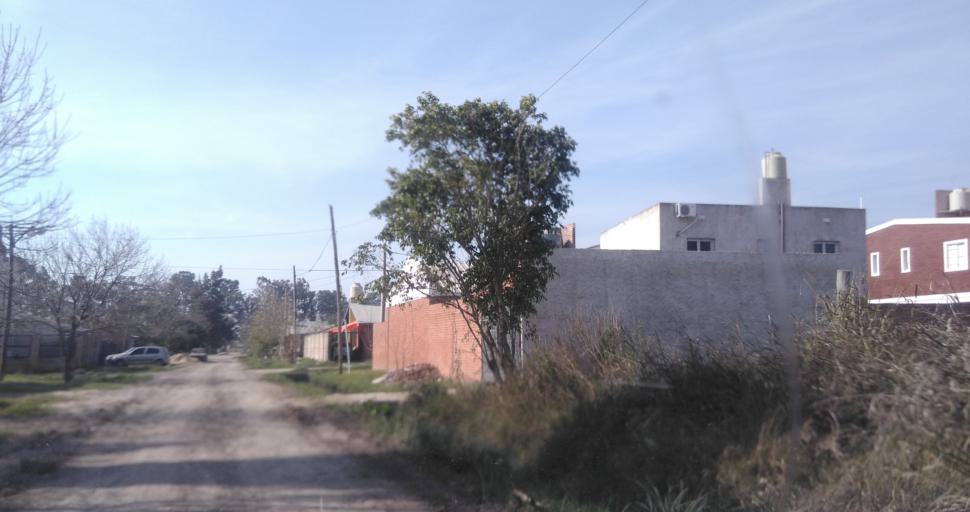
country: AR
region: Chaco
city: Fontana
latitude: -27.4439
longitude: -59.0326
